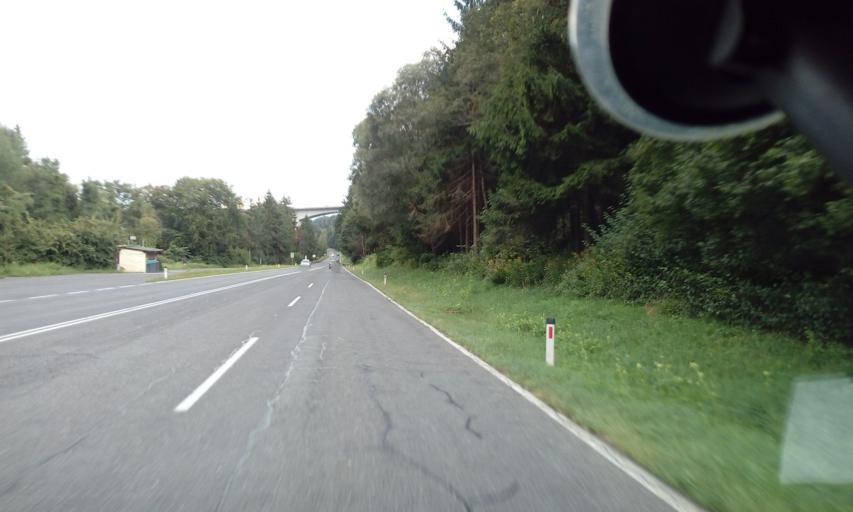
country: AT
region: Carinthia
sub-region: Villach Stadt
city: Villach
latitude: 46.6452
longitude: 13.7972
